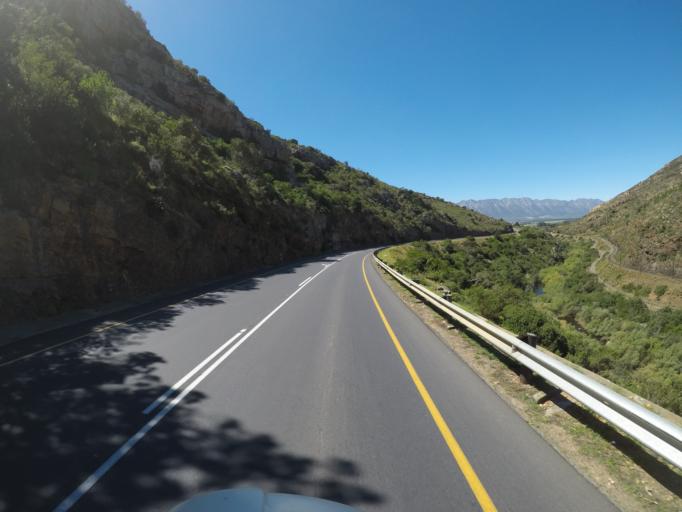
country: ZA
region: Western Cape
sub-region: Cape Winelands District Municipality
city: Ceres
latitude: -33.3172
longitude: 19.0853
